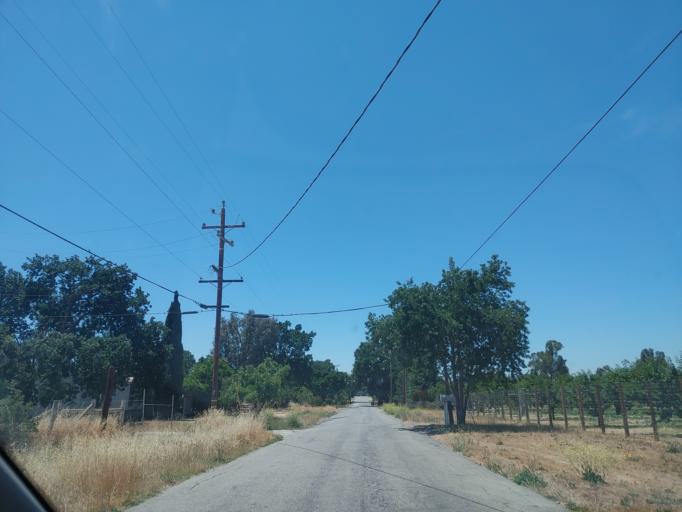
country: US
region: California
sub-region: San Benito County
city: Hollister
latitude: 36.9189
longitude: -121.3449
